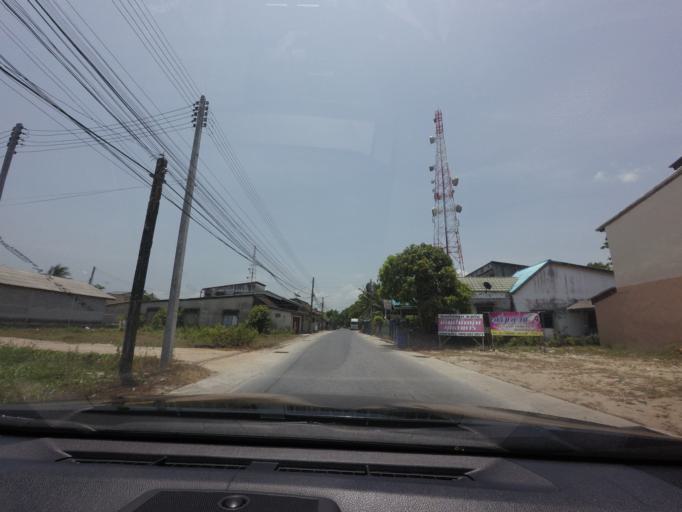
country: TH
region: Pattani
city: Yaring
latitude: 6.8633
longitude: 101.3679
